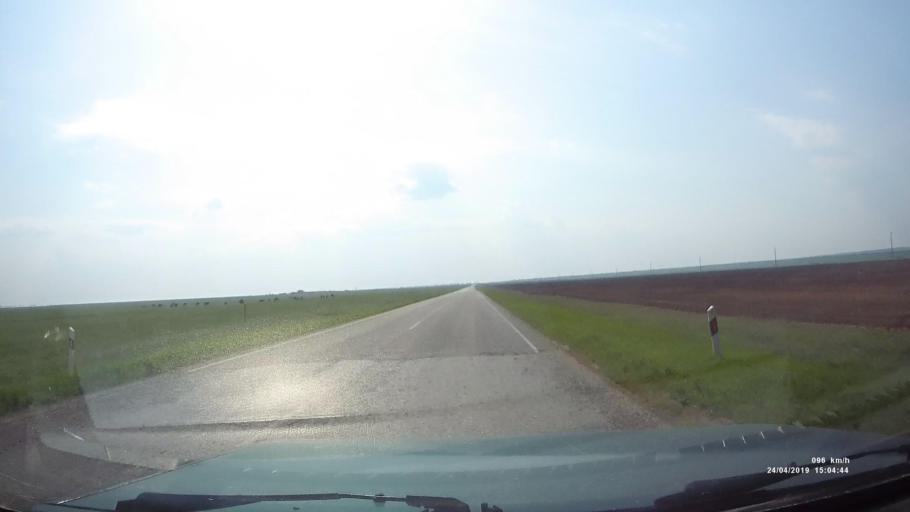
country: RU
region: Rostov
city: Remontnoye
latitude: 46.5613
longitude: 43.4643
